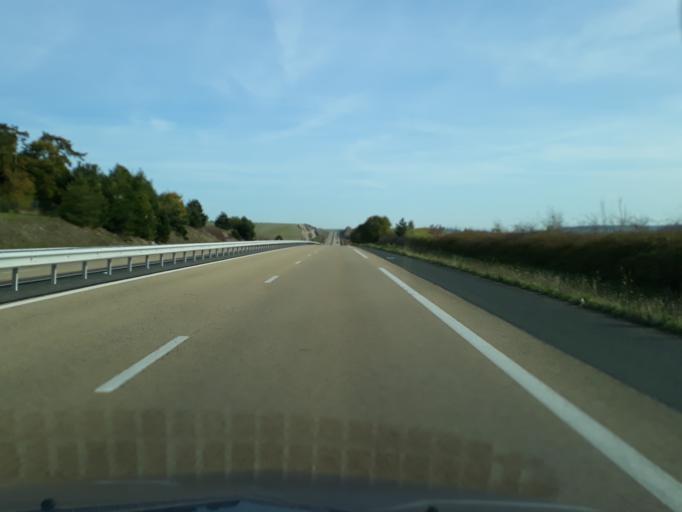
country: FR
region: Champagne-Ardenne
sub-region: Departement de l'Aube
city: Estissac
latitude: 48.2708
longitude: 3.7668
